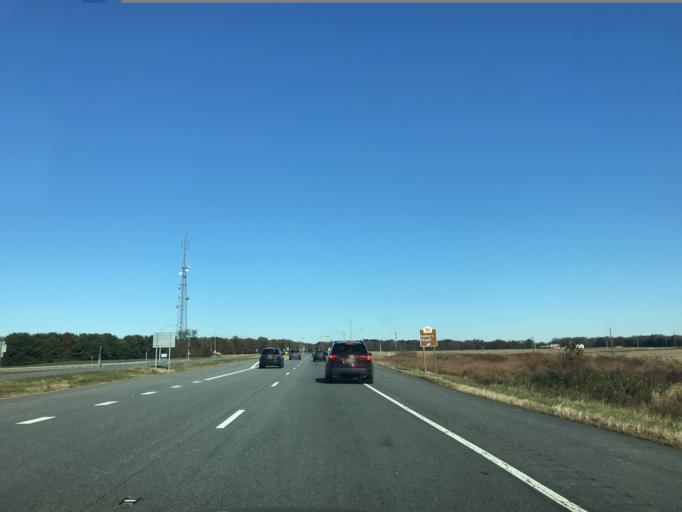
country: US
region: Maryland
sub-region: Queen Anne's County
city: Kingstown
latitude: 39.1712
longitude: -75.9179
